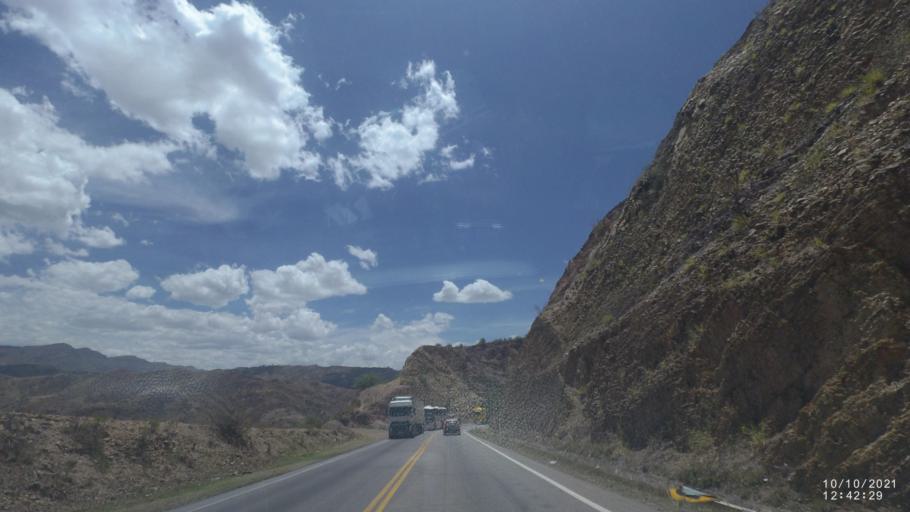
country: BO
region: Cochabamba
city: Irpa Irpa
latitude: -17.6290
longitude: -66.3929
